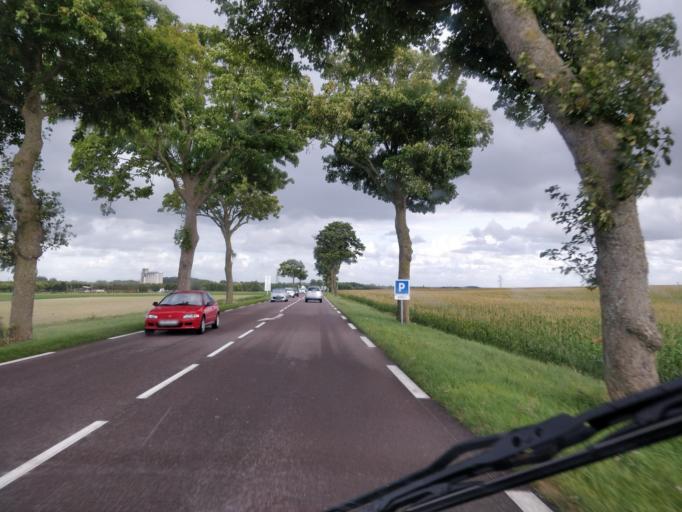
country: FR
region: Champagne-Ardenne
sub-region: Departement de l'Aube
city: Saint-Parres-aux-Tertres
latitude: 48.2900
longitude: 4.1543
